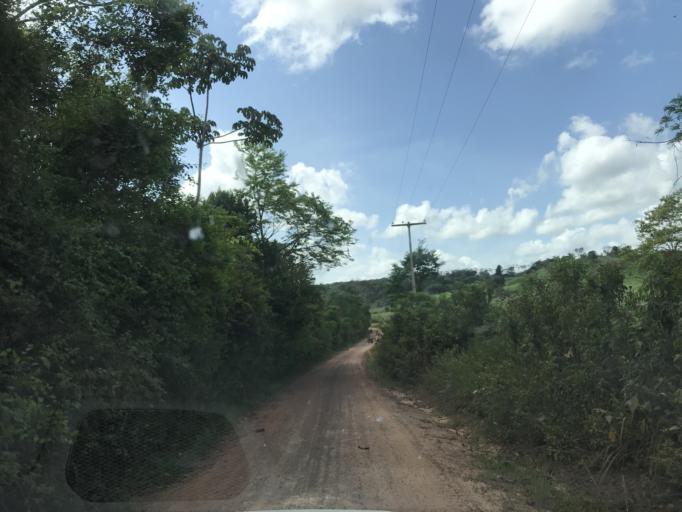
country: BR
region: Bahia
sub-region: Entre Rios
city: Entre Rios
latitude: -12.1732
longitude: -38.0628
